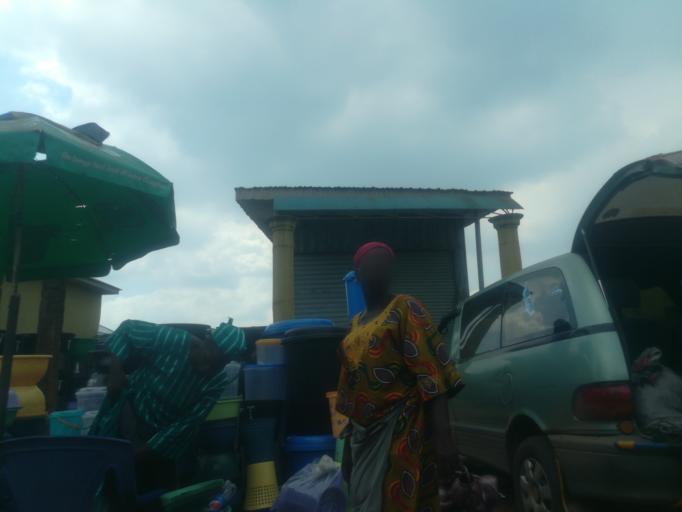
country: NG
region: Oyo
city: Ibadan
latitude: 7.3939
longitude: 3.9586
